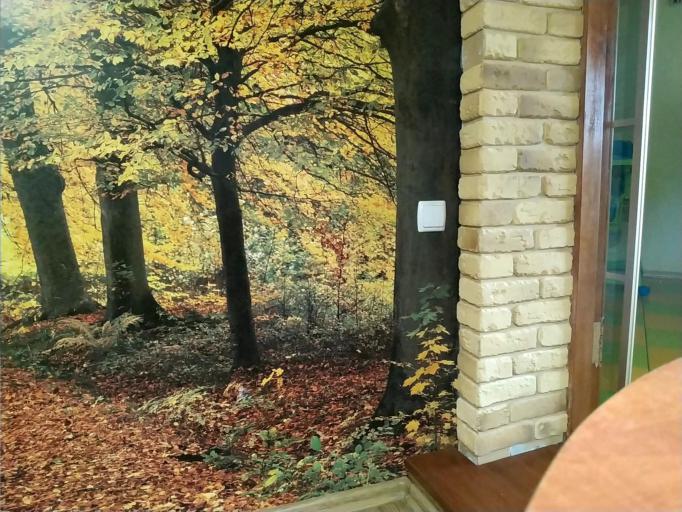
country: RU
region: Smolensk
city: Dorogobuzh
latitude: 54.9223
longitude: 33.3243
